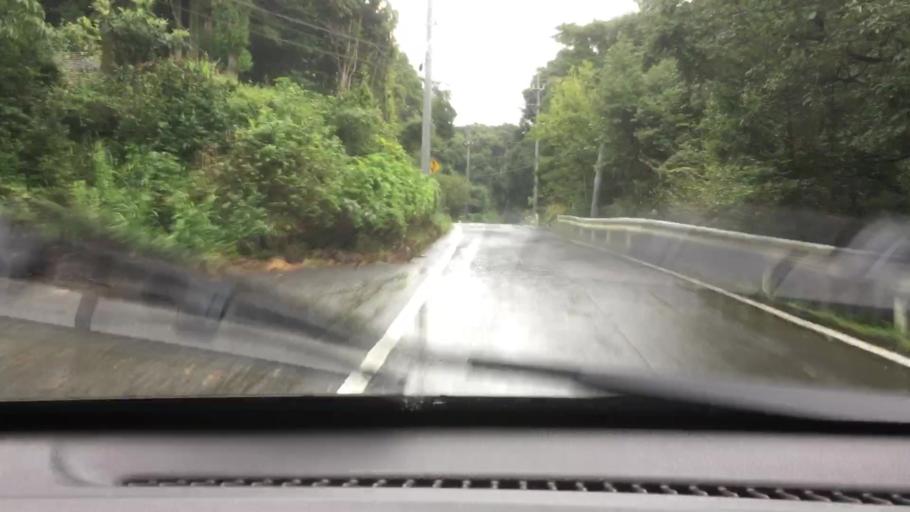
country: JP
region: Nagasaki
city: Togitsu
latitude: 32.8759
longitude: 129.7587
